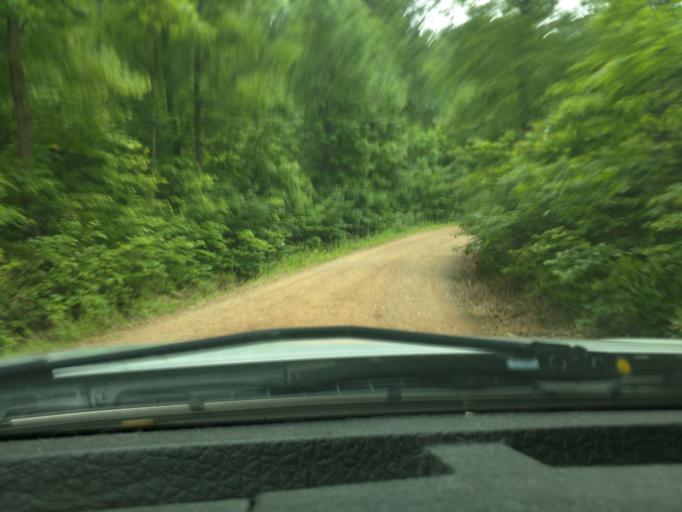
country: US
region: Arkansas
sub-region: Madison County
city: Huntsville
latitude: 35.8765
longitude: -93.5245
